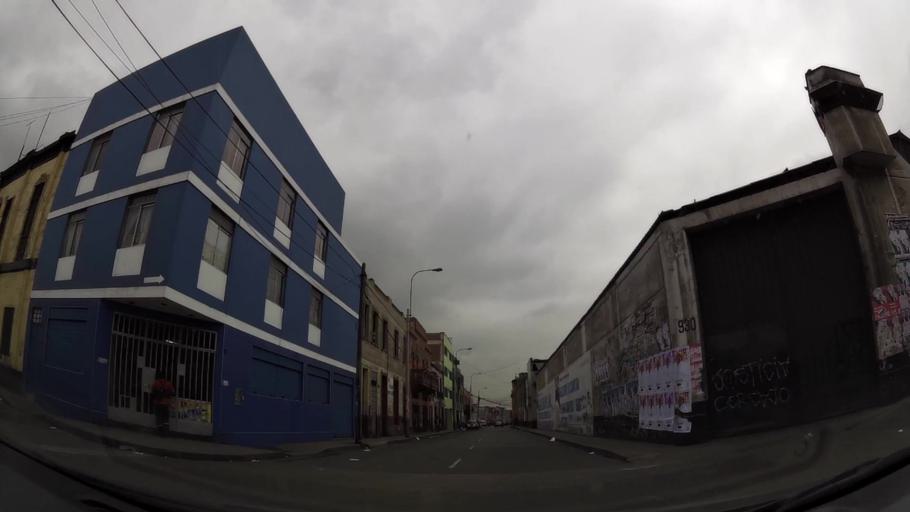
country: PE
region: Lima
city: Lima
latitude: -12.0421
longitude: -77.0401
